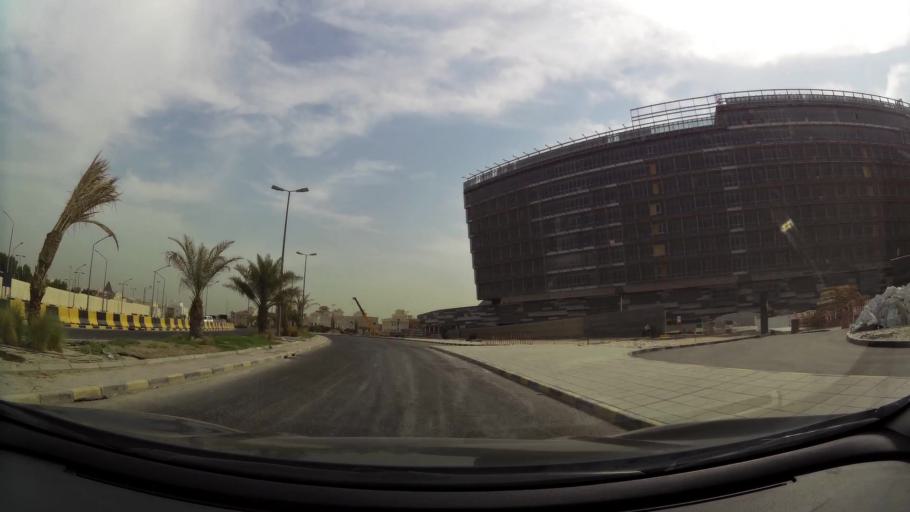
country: KW
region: Mubarak al Kabir
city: Sabah as Salim
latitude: 29.2738
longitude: 48.0196
